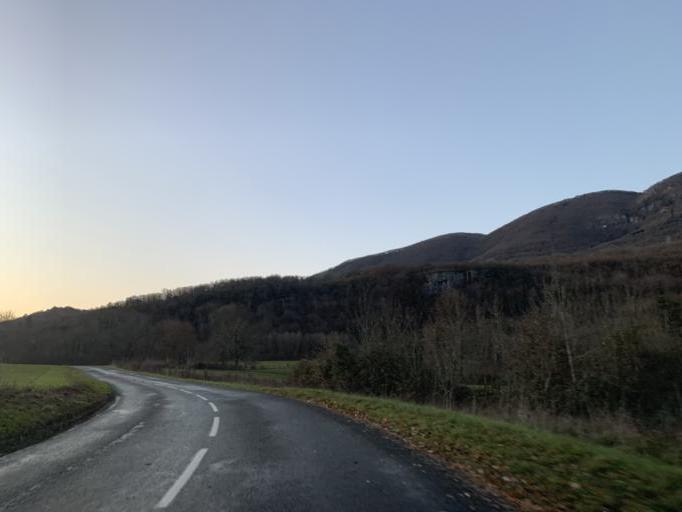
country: FR
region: Rhone-Alpes
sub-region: Departement de l'Ain
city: Virieu-le-Grand
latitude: 45.8181
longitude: 5.6116
